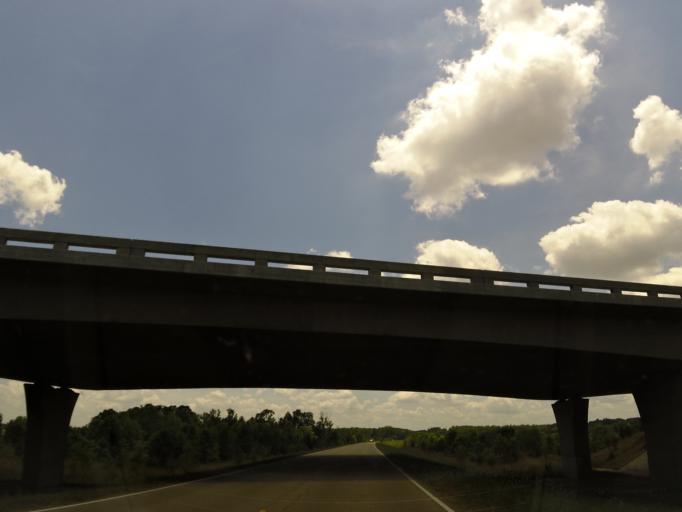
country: US
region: Mississippi
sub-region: Lee County
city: Tupelo
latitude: 34.3163
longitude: -88.7172
